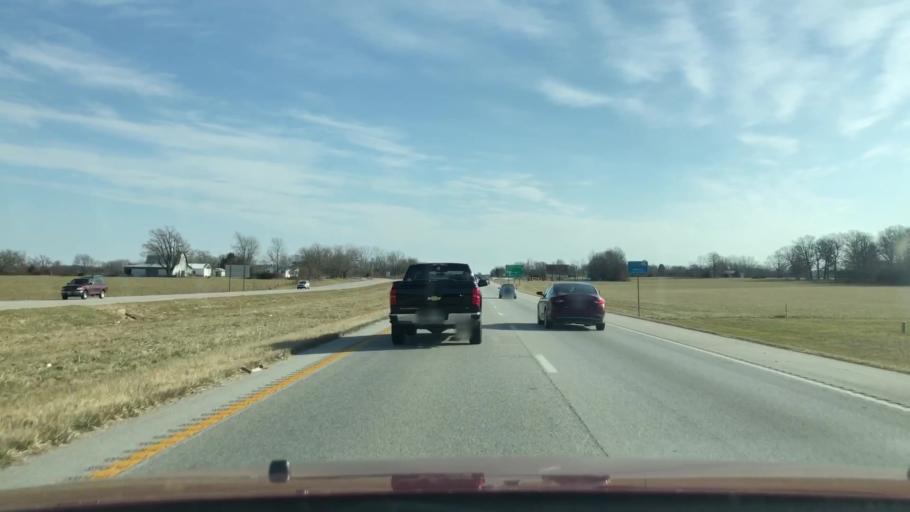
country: US
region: Missouri
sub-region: Webster County
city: Rogersville
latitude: 37.1183
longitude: -93.1062
